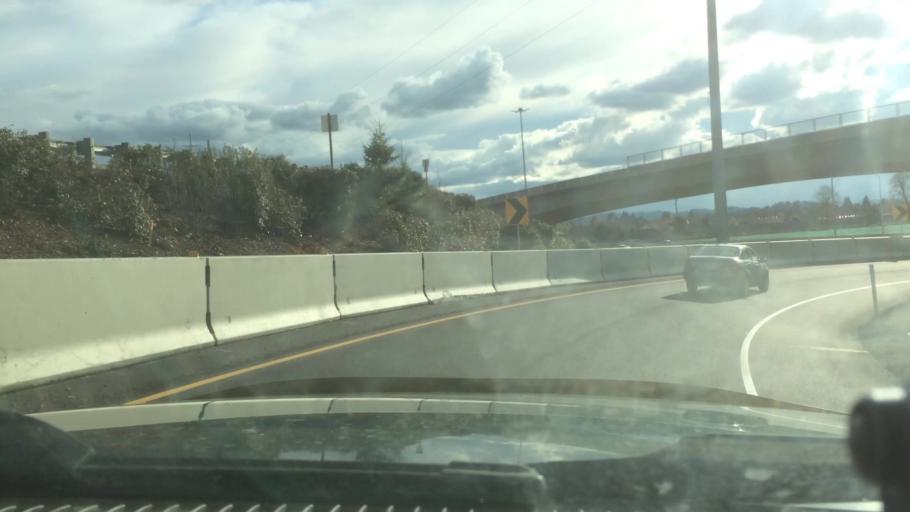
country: US
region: Oregon
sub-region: Lane County
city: Springfield
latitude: 44.0830
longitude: -123.0453
